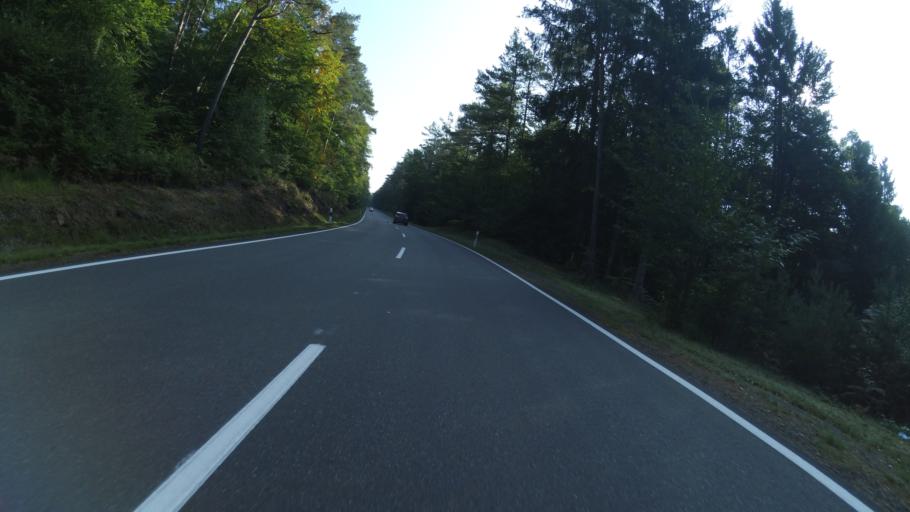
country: DE
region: Rheinland-Pfalz
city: Langwieden
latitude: 49.3975
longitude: 7.5228
